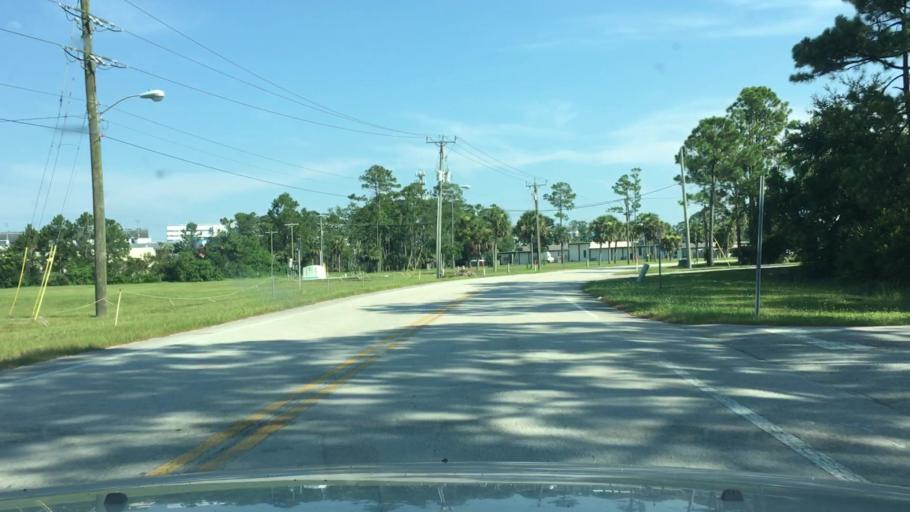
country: US
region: Florida
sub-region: Volusia County
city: Daytona Beach
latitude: 29.1942
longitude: -81.0792
